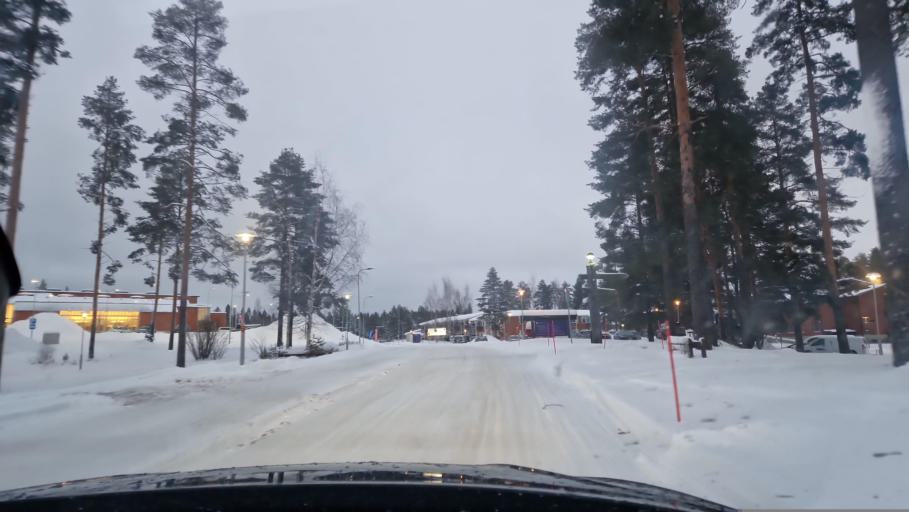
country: FI
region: Kainuu
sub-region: Kajaani
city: Vuokatti
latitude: 64.1379
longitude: 28.2858
